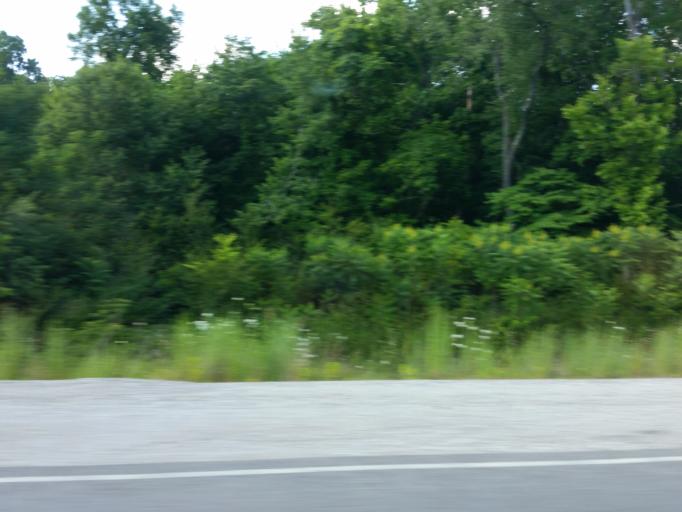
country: US
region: Tennessee
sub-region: Lewis County
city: Hohenwald
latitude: 35.5631
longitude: -87.3841
